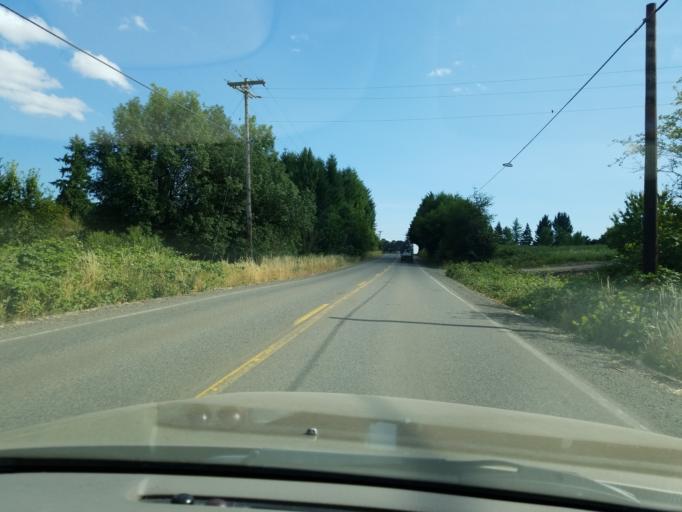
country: US
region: Oregon
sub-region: Yamhill County
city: Carlton
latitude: 45.2792
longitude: -123.2035
